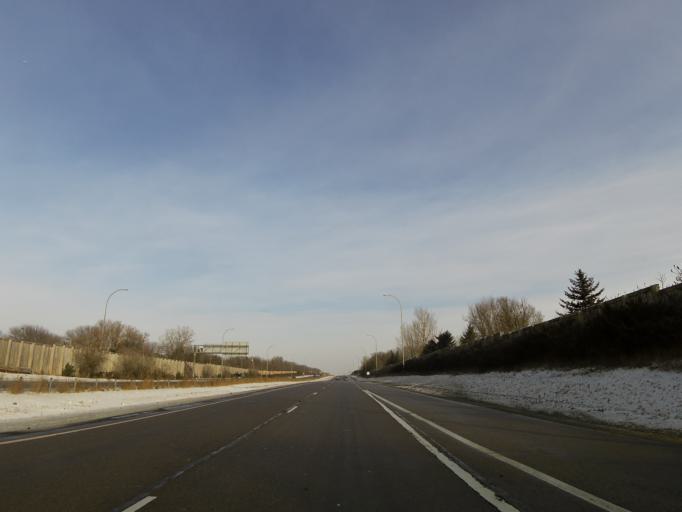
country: US
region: Minnesota
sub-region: Scott County
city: Savage
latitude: 44.8219
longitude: -93.3981
